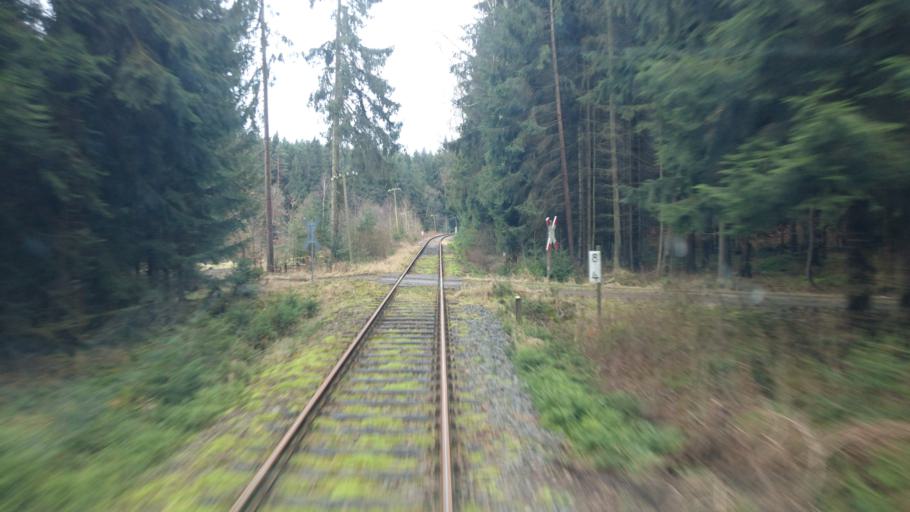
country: DE
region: Thuringia
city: Kirschkau
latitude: 50.5740
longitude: 11.8924
